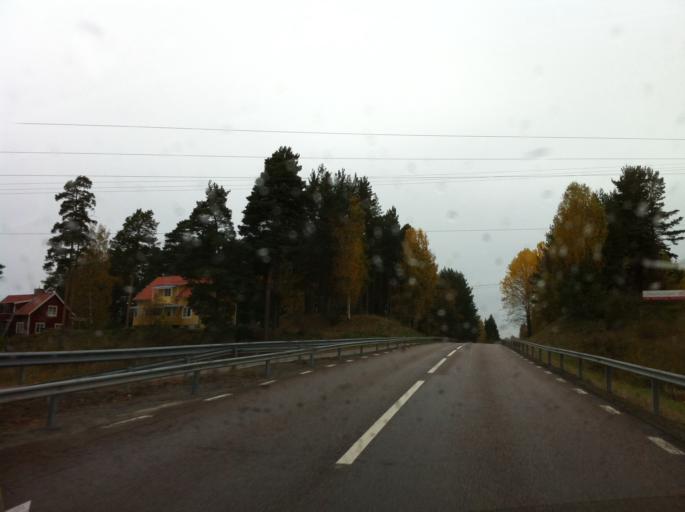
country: SE
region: Dalarna
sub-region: Ludvika Kommun
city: Grangesberg
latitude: 60.2591
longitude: 14.9840
